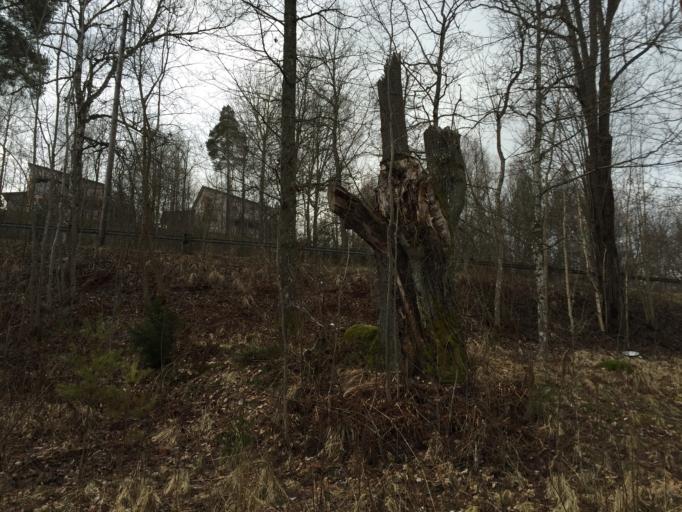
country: SE
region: Stockholm
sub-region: Salems Kommun
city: Ronninge
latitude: 59.1952
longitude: 17.7298
